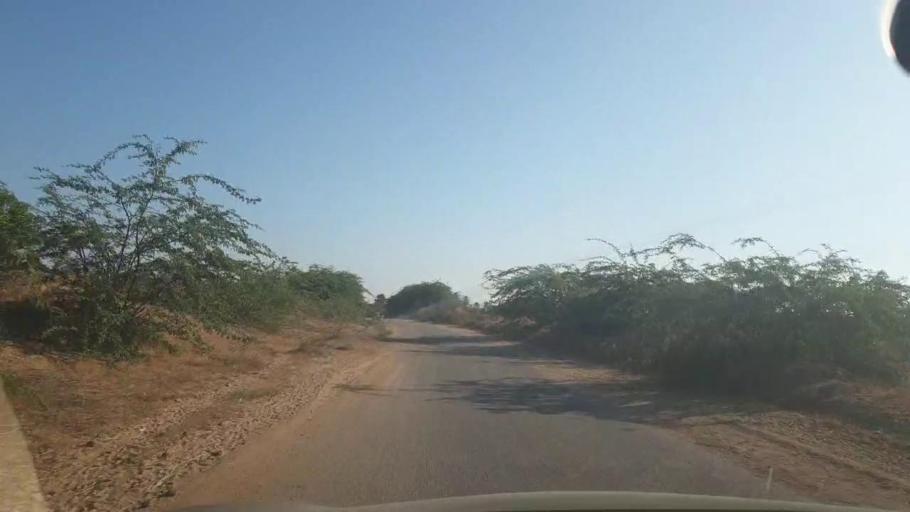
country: PK
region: Sindh
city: Malir Cantonment
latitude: 25.1151
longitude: 67.2740
